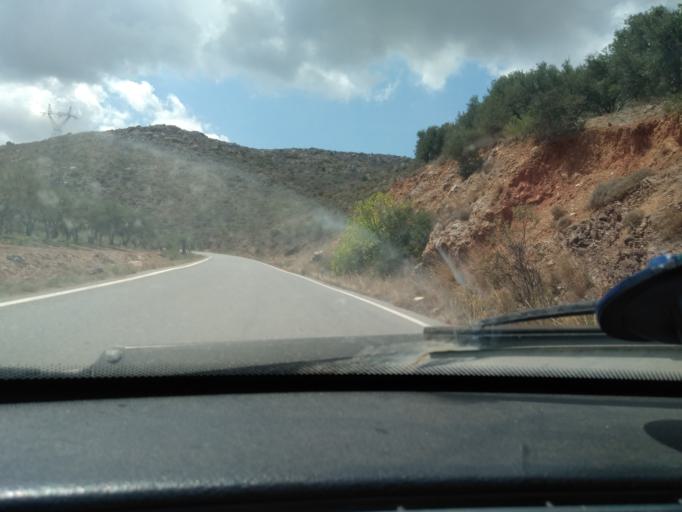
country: GR
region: Crete
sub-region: Nomos Lasithiou
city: Siteia
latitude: 35.1142
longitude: 26.0567
